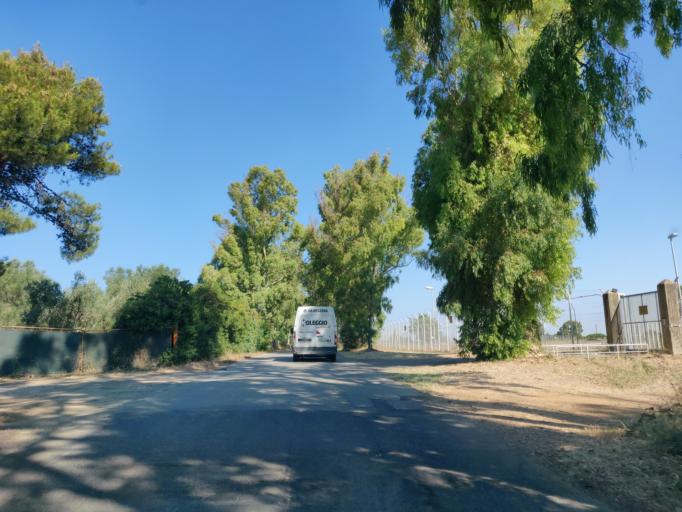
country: IT
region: Latium
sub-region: Citta metropolitana di Roma Capitale
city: Aurelia
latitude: 42.1637
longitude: 11.7441
